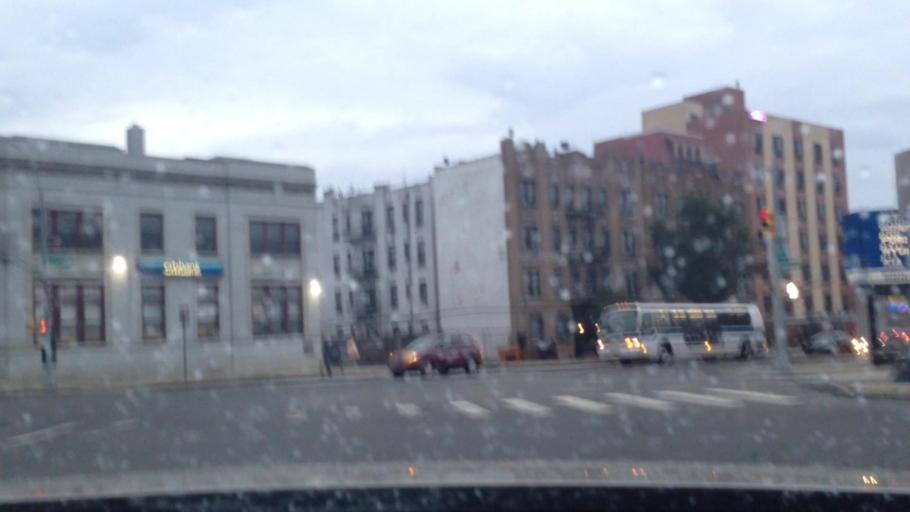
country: US
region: New York
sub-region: Kings County
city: East New York
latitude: 40.6782
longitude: -73.8979
